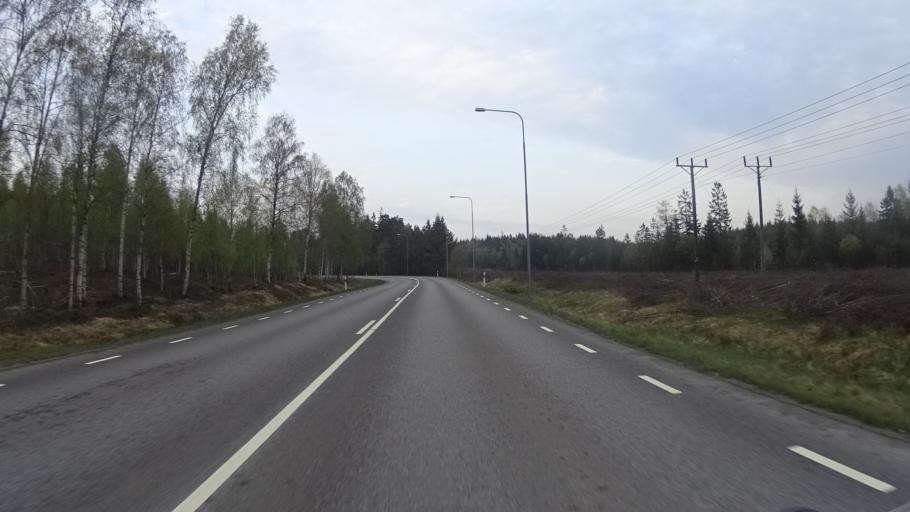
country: SE
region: Kronoberg
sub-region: Ljungby Kommun
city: Ljungby
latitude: 56.8300
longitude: 13.9730
